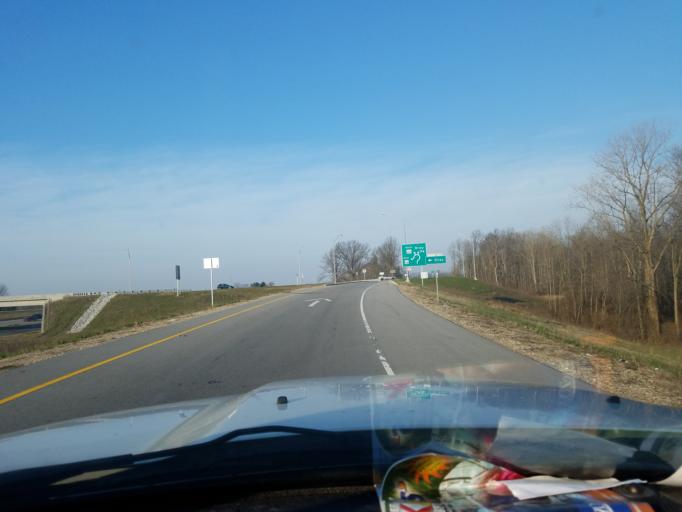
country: US
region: Indiana
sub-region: Vigo County
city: Terre Haute
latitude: 39.4146
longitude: -87.3350
